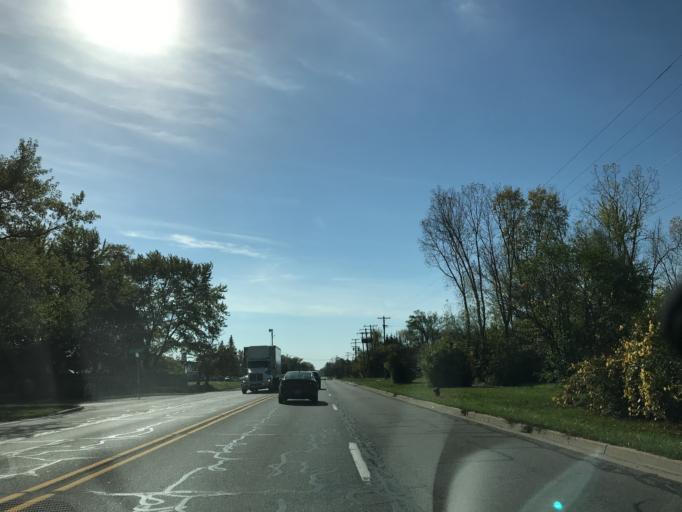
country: US
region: Michigan
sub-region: Oakland County
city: Farmington
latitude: 42.4745
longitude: -83.3380
